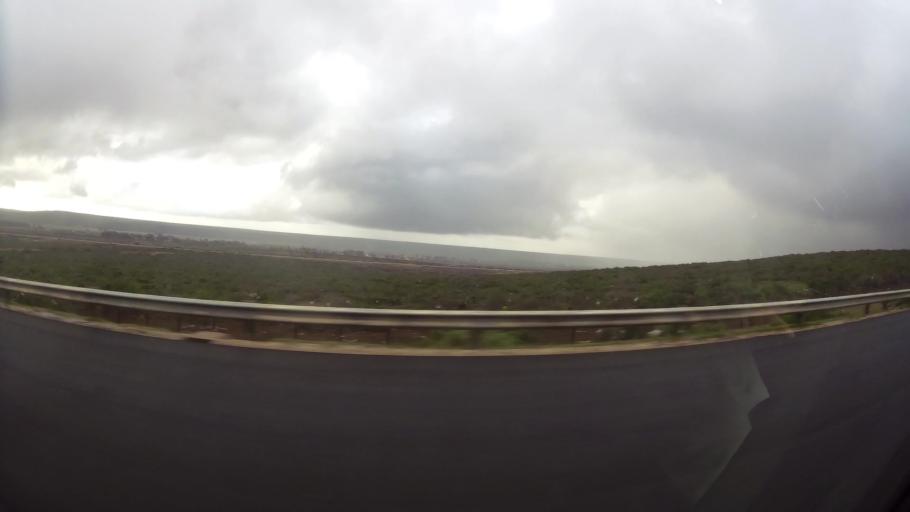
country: ZA
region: Eastern Cape
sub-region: Nelson Mandela Bay Metropolitan Municipality
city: Port Elizabeth
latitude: -33.8263
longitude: 25.5099
